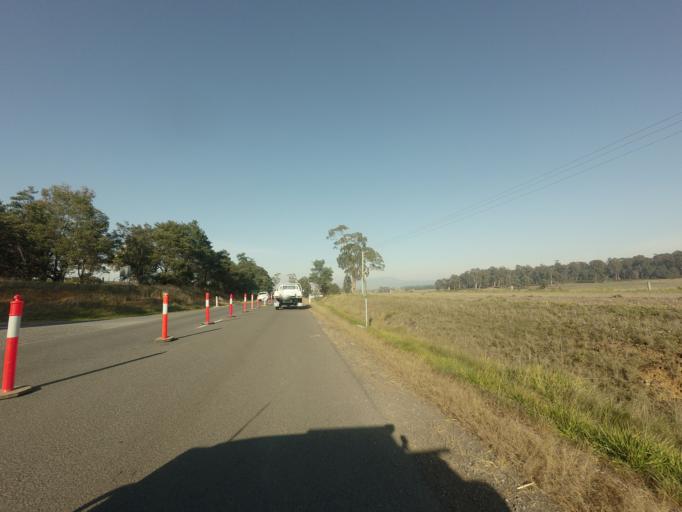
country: AU
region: Tasmania
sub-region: Northern Midlands
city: Longford
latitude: -41.5551
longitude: 146.9878
